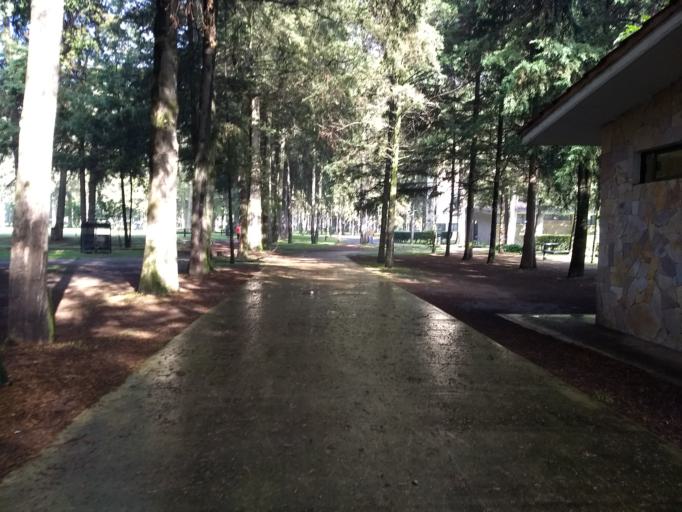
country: MX
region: Mexico
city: Toluca
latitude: 19.2707
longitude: -99.6502
